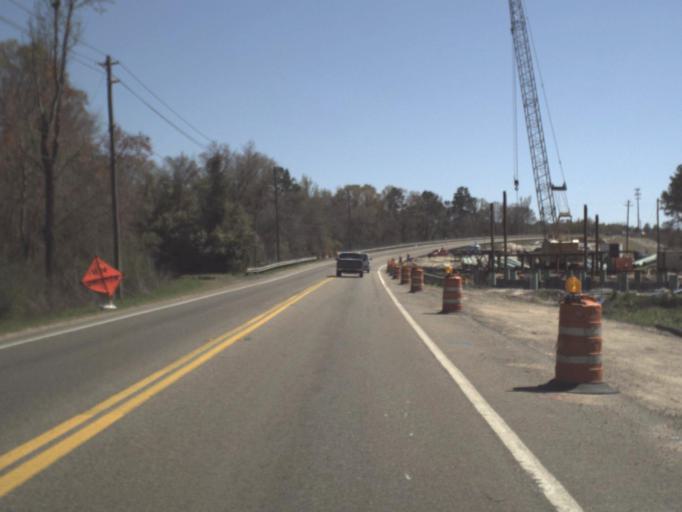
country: US
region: Florida
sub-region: Leon County
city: Tallahassee
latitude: 30.4458
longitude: -84.3546
